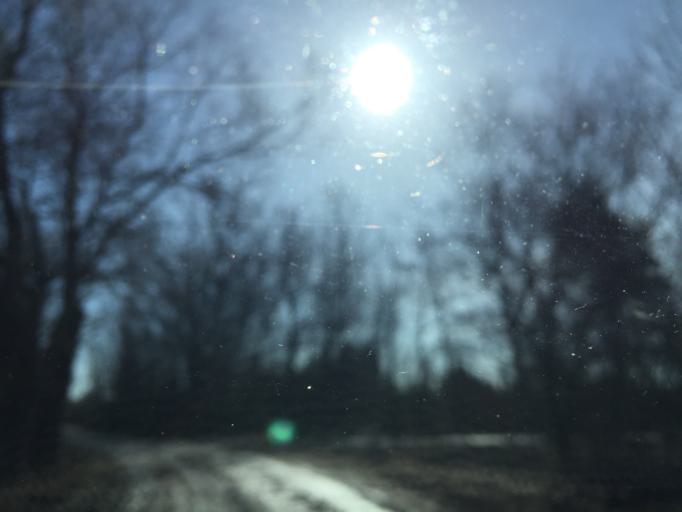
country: EE
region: Laeaene
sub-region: Haapsalu linn
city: Haapsalu
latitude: 58.6836
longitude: 23.5125
